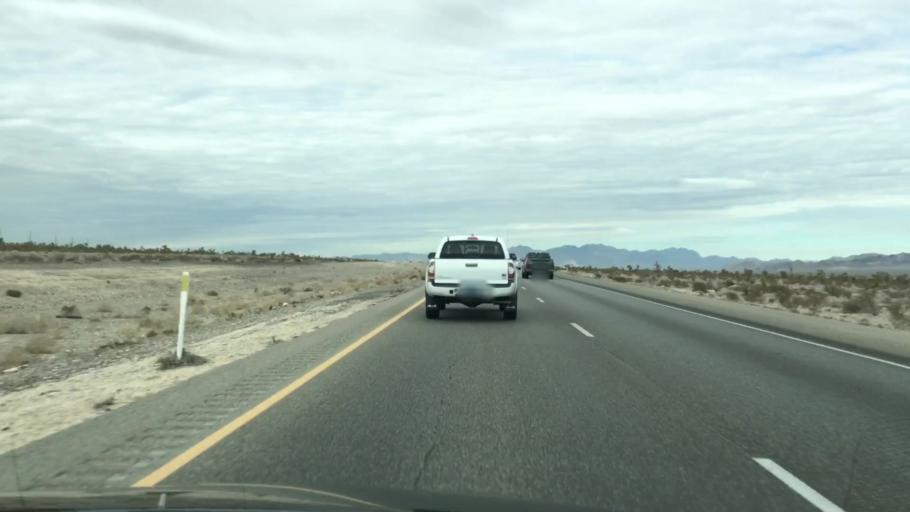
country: US
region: Nevada
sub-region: Clark County
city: Summerlin South
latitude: 36.4563
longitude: -115.4410
